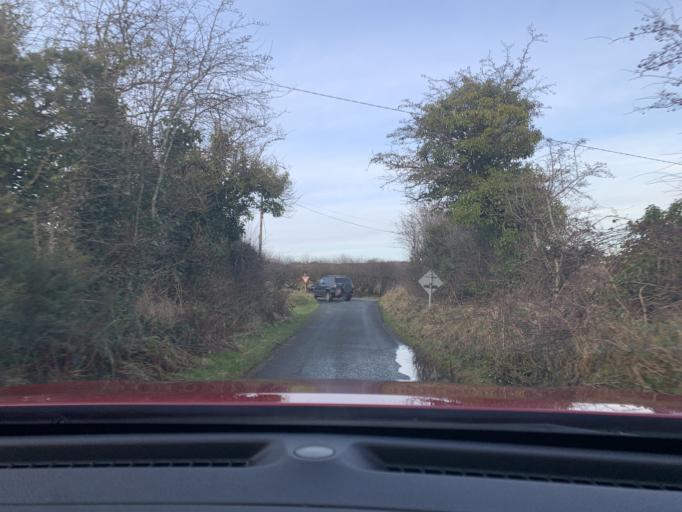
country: IE
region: Connaught
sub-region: Sligo
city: Strandhill
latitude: 54.1754
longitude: -8.6574
